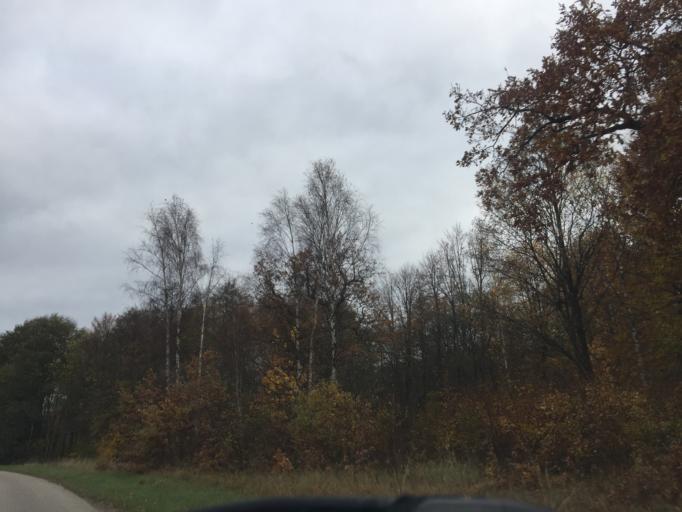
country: LV
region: Liepaja
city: Vec-Liepaja
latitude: 56.5474
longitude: 21.0784
